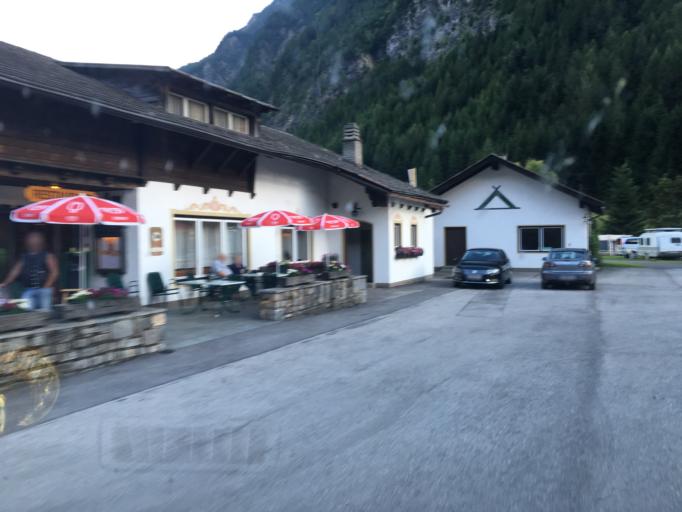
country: AT
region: Carinthia
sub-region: Politischer Bezirk Spittal an der Drau
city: Heiligenblut
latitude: 47.0375
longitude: 12.8392
